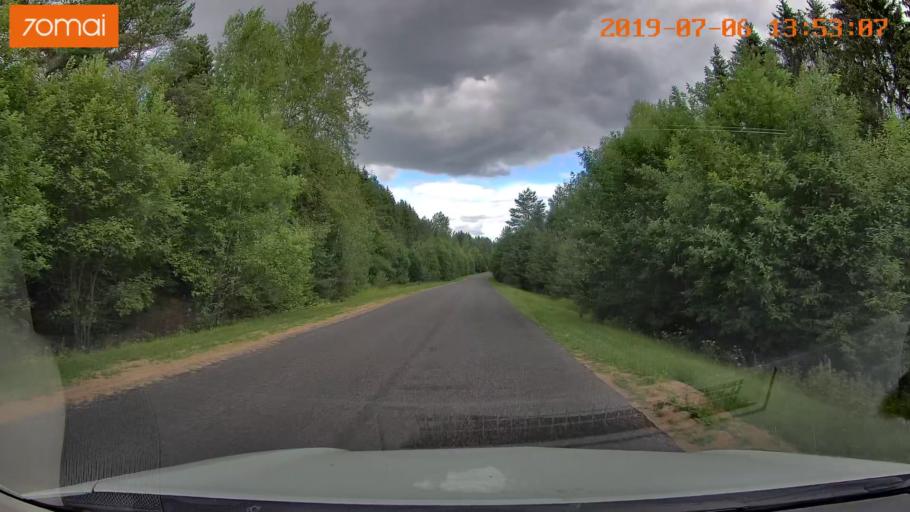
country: BY
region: Minsk
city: Ivyanyets
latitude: 53.7296
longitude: 26.8261
